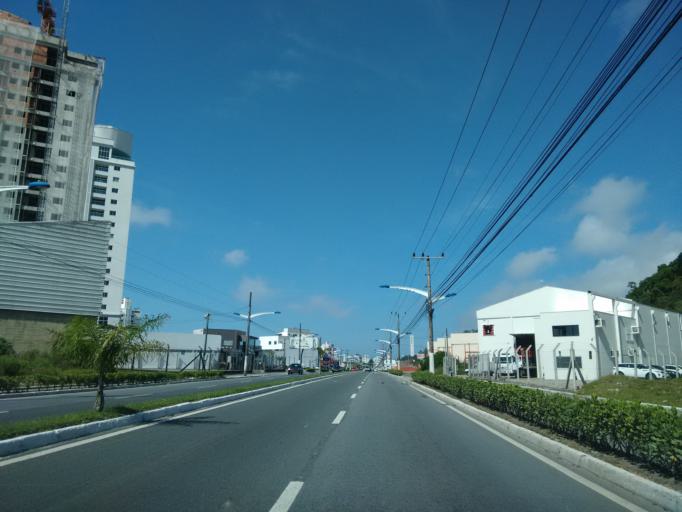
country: BR
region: Santa Catarina
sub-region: Itajai
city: Itajai
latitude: -26.9276
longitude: -48.6821
